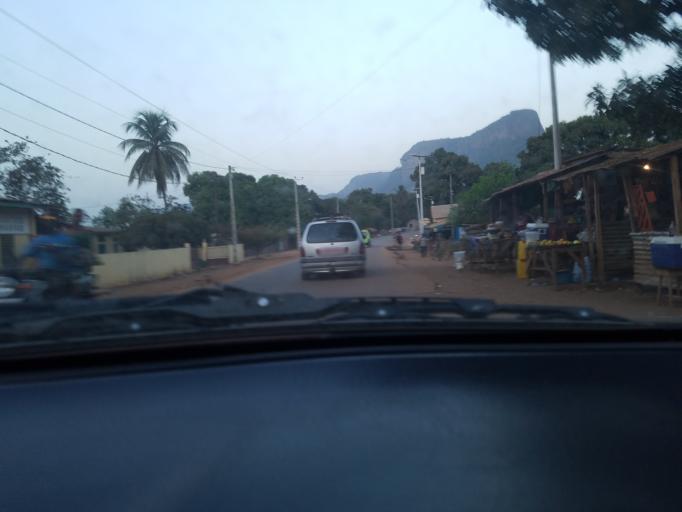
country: GN
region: Kindia
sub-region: Prefecture de Dubreka
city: Dubreka
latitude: 9.7898
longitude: -13.4935
